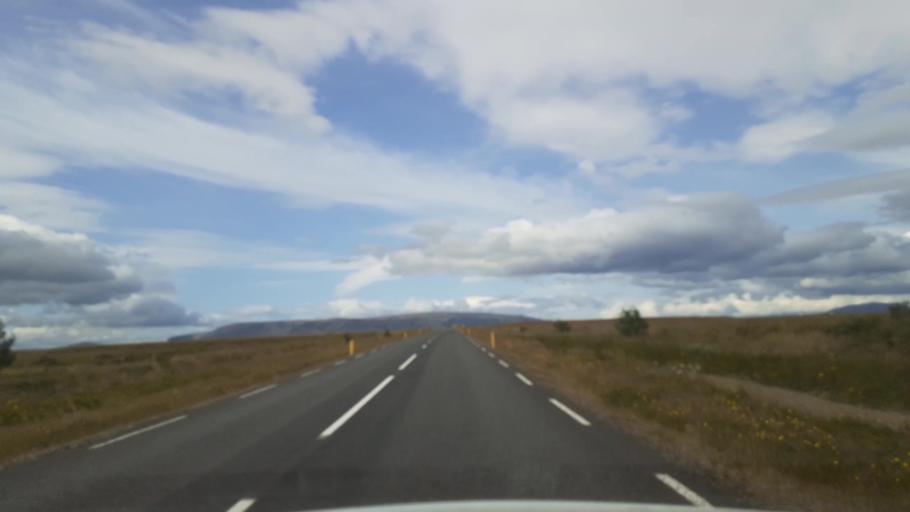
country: IS
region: South
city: Selfoss
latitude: 63.9156
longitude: -20.8391
